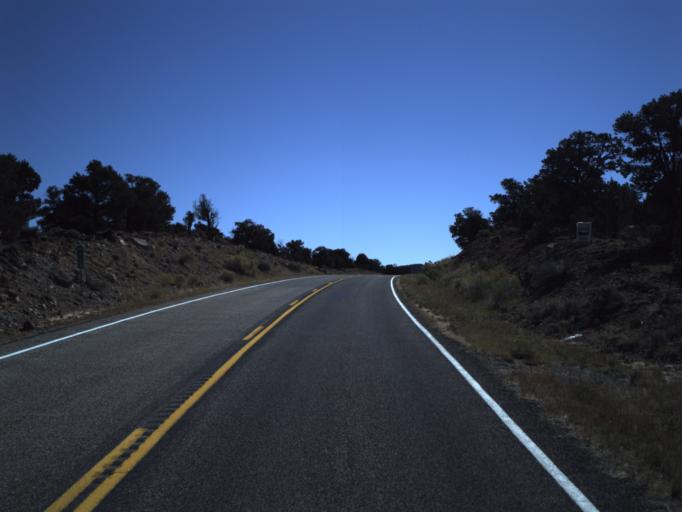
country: US
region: Utah
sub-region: Wayne County
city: Loa
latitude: 38.2310
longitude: -111.3603
